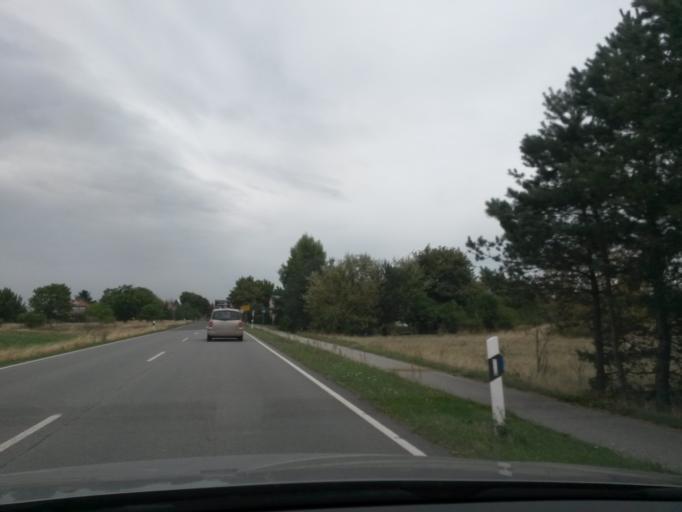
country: DE
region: Saxony-Anhalt
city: Klietz
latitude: 52.6917
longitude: 12.0676
